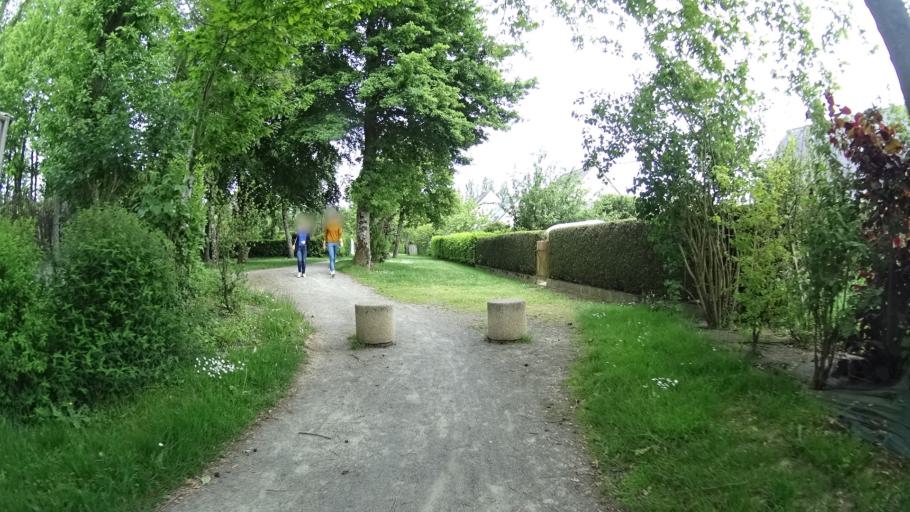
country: FR
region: Brittany
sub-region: Departement d'Ille-et-Vilaine
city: La Meziere
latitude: 48.2163
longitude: -1.7575
